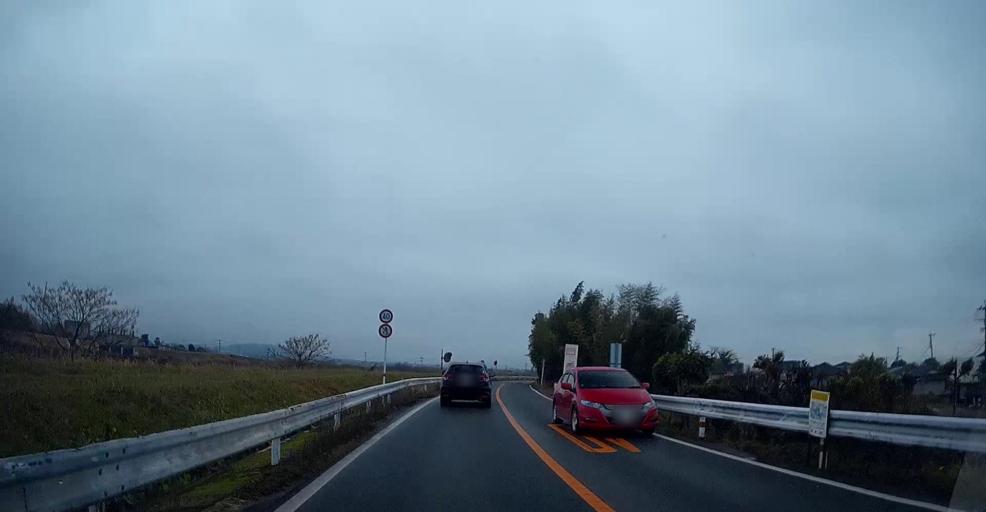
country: JP
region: Kumamoto
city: Kumamoto
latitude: 32.7562
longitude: 130.7488
